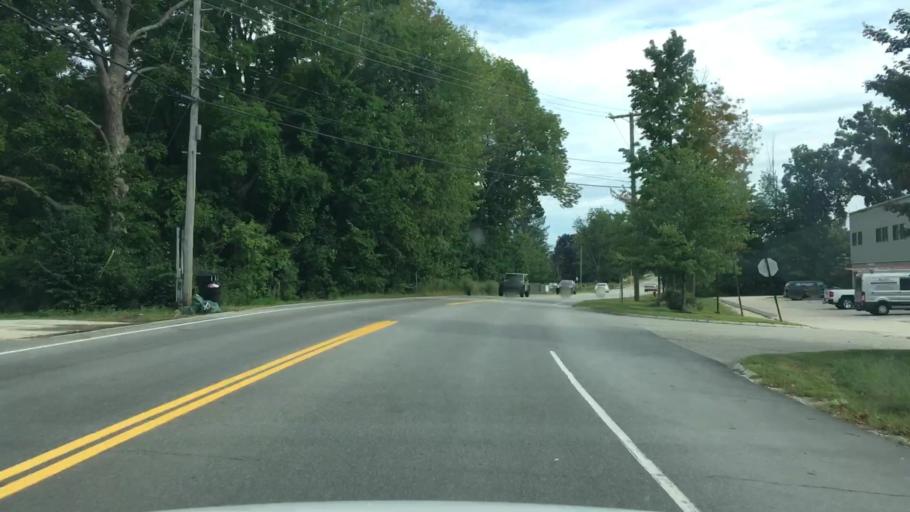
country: US
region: New Hampshire
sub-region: Strafford County
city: Dover
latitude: 43.1890
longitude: -70.9006
